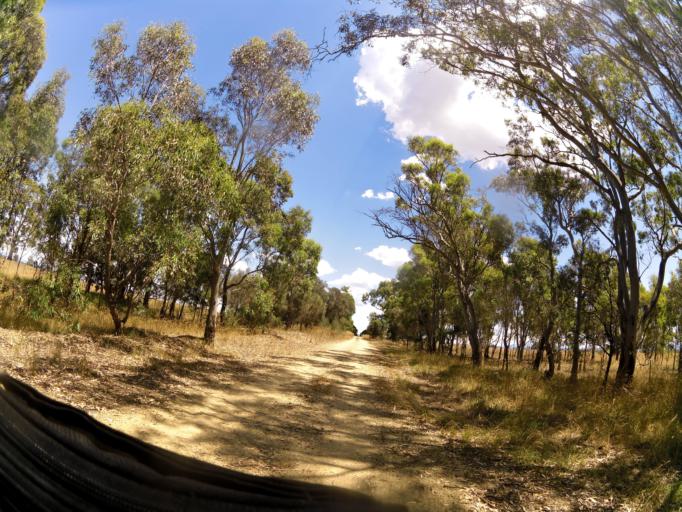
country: AU
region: Victoria
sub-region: Wellington
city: Heyfield
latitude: -37.9820
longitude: 146.8337
